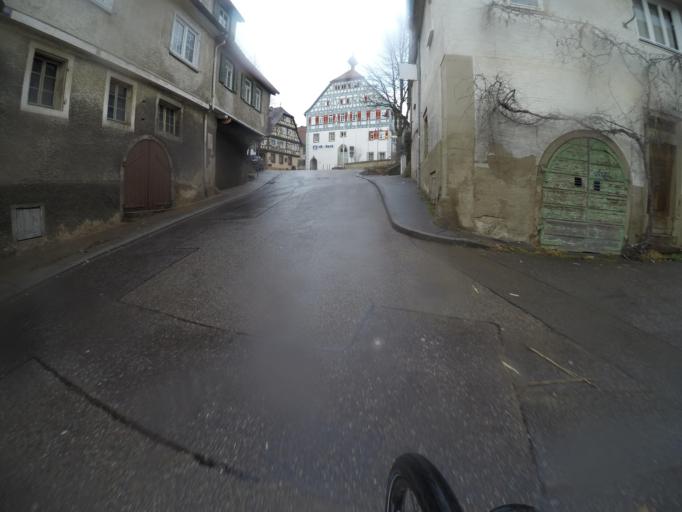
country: DE
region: Baden-Wuerttemberg
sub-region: Regierungsbezirk Stuttgart
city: Vaihingen an der Enz
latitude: 48.9164
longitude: 8.9851
